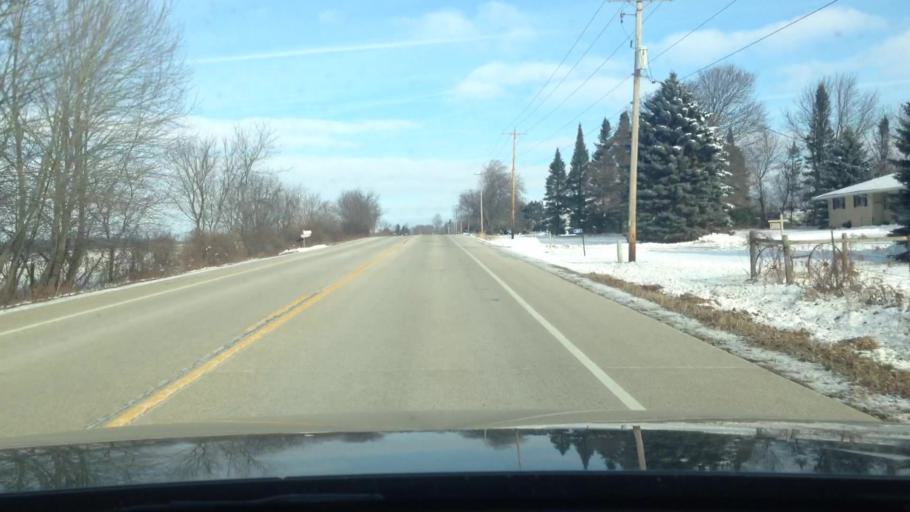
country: US
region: Wisconsin
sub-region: Walworth County
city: Lake Geneva
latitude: 42.6624
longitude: -88.4138
